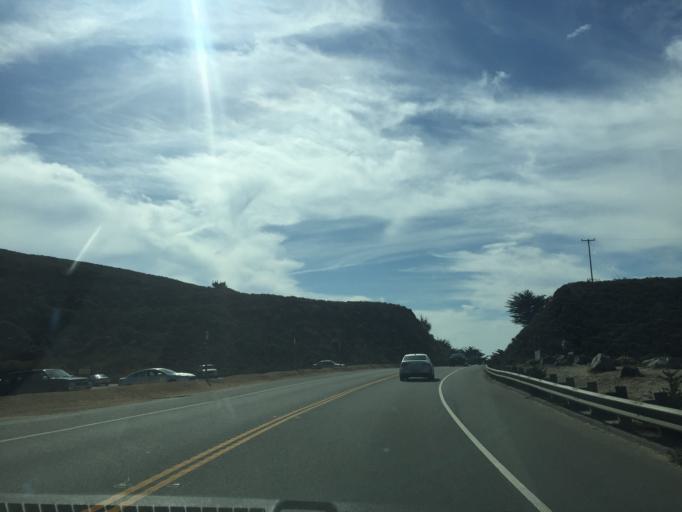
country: US
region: California
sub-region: San Mateo County
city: Montara
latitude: 37.5638
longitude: -122.5127
